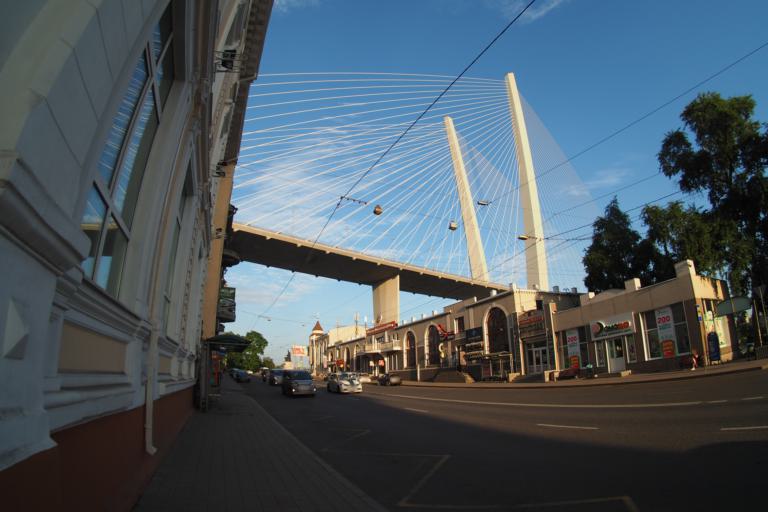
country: RU
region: Primorskiy
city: Vladivostok
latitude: 43.1141
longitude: 131.8949
